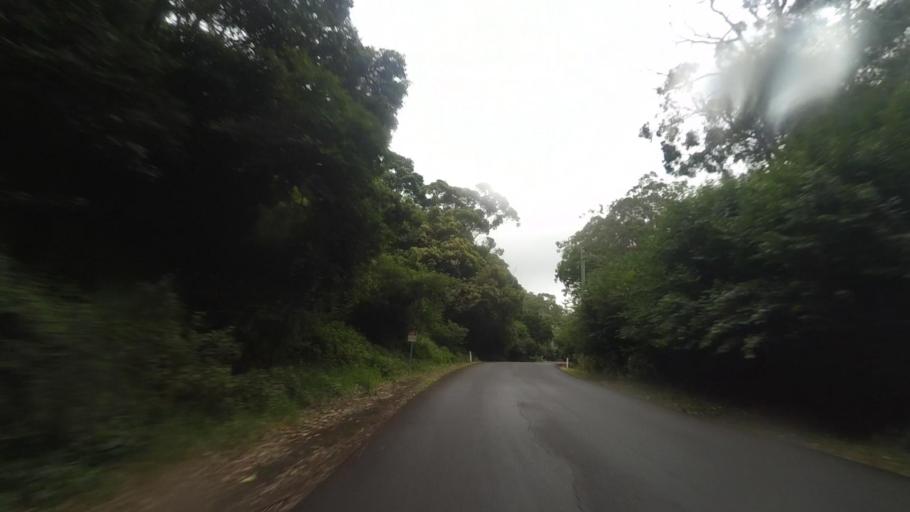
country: AU
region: New South Wales
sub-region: Wollongong
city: Cordeaux Heights
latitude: -34.4243
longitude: 150.8129
